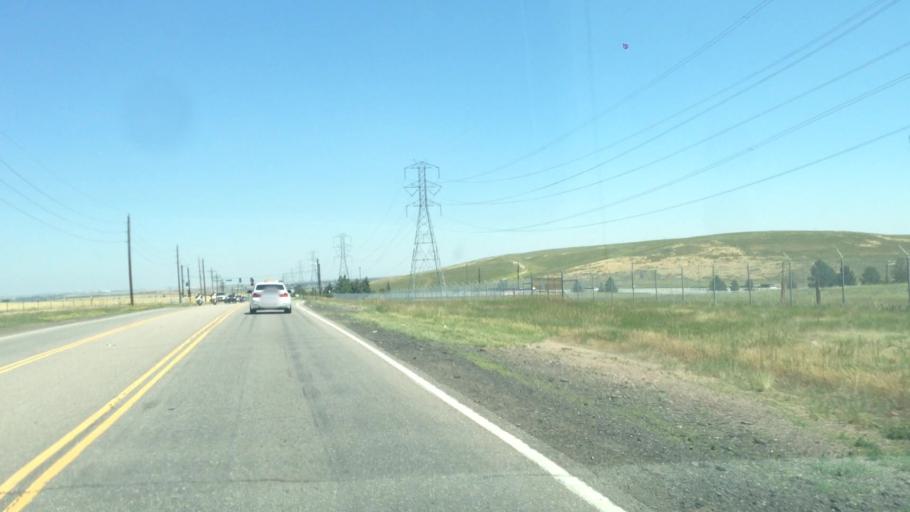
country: US
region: Colorado
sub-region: Arapahoe County
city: Dove Valley
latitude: 39.6502
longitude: -104.7162
